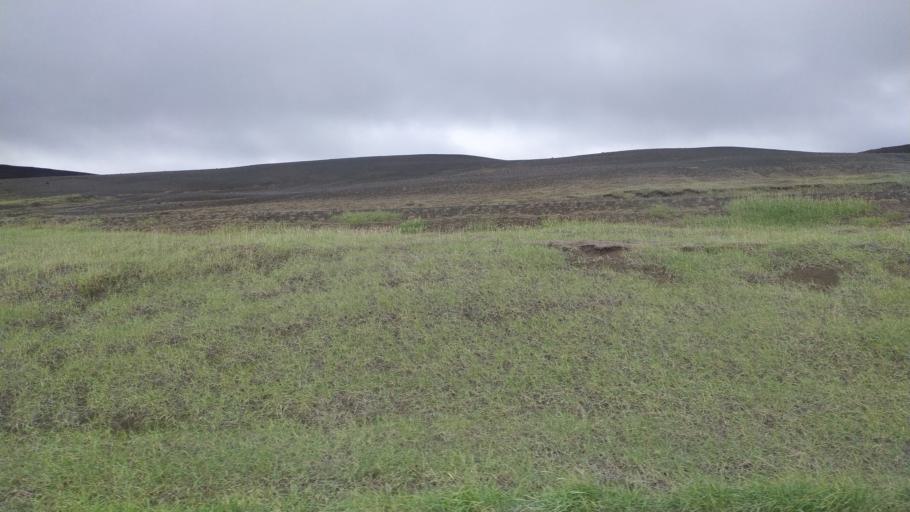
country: IS
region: Northeast
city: Laugar
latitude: 65.5239
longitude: -15.9884
